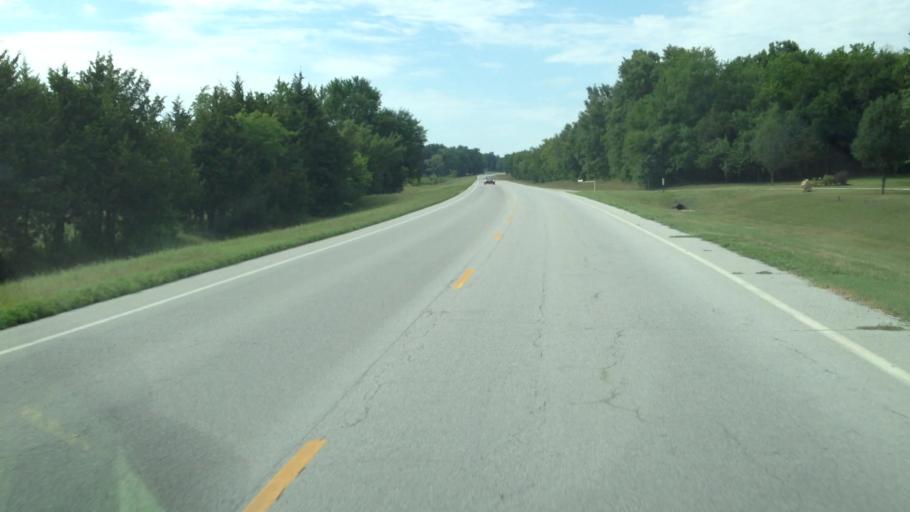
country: US
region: Kansas
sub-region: Labette County
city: Oswego
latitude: 37.1486
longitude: -95.1045
